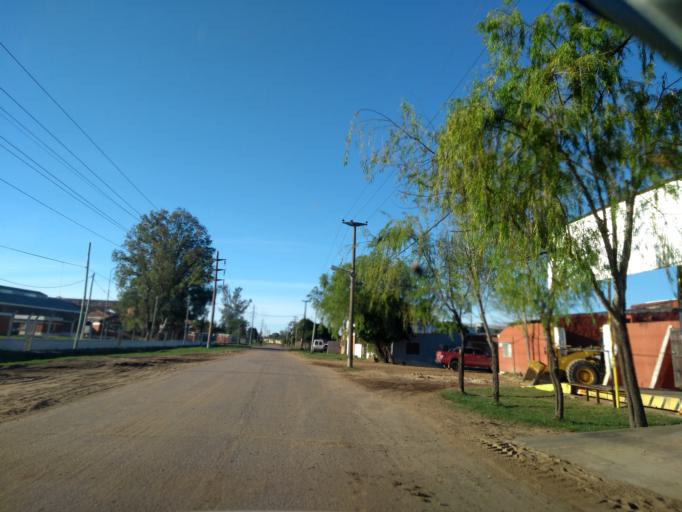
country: AR
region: Chaco
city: Barranqueras
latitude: -27.4971
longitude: -58.9313
